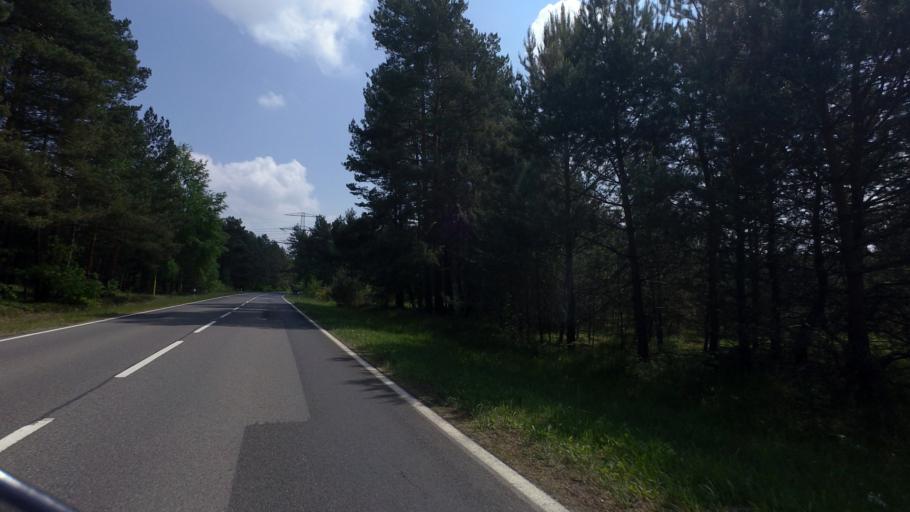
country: DE
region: Saxony
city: Schleife
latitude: 51.5631
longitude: 14.4888
